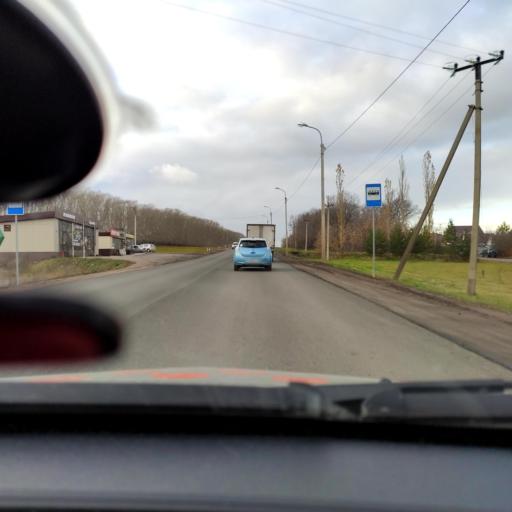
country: RU
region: Bashkortostan
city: Kabakovo
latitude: 54.6261
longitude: 56.1044
